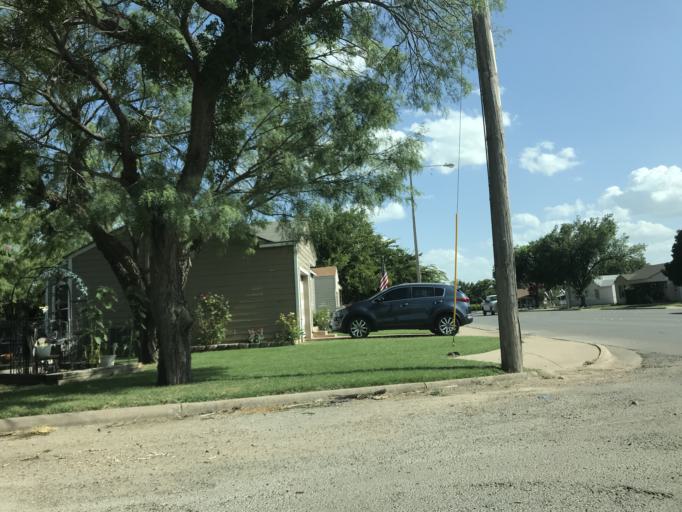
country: US
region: Texas
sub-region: Taylor County
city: Abilene
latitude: 32.4297
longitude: -99.7593
